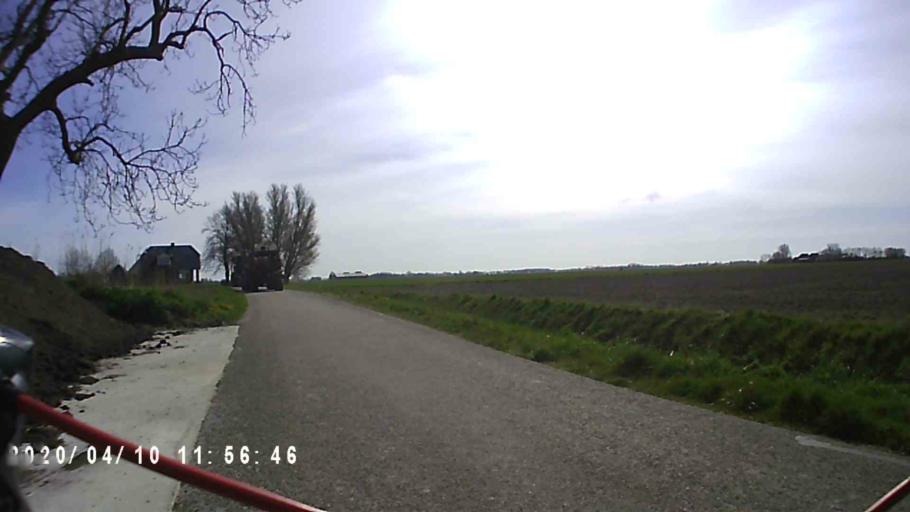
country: NL
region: Groningen
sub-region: Gemeente De Marne
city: Ulrum
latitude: 53.3868
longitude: 6.3493
